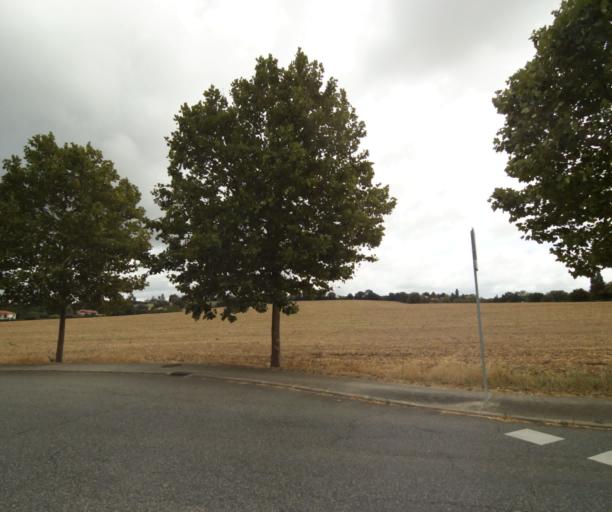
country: FR
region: Midi-Pyrenees
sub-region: Departement de la Haute-Garonne
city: Balma
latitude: 43.5907
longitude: 1.5114
